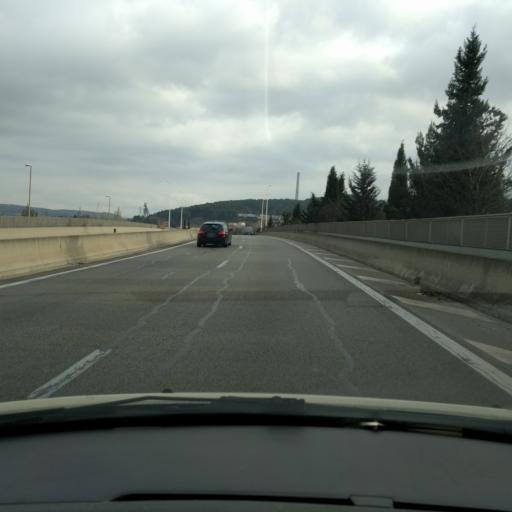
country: FR
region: Provence-Alpes-Cote d'Azur
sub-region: Departement des Bouches-du-Rhone
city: Gardanne
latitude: 43.4566
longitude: 5.4619
